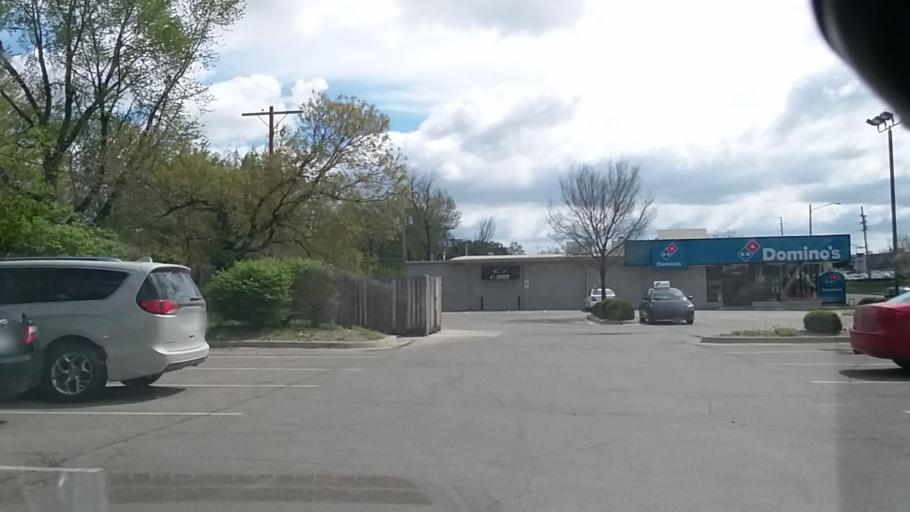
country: US
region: Kansas
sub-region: Douglas County
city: Lawrence
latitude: 38.9432
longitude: -95.2489
